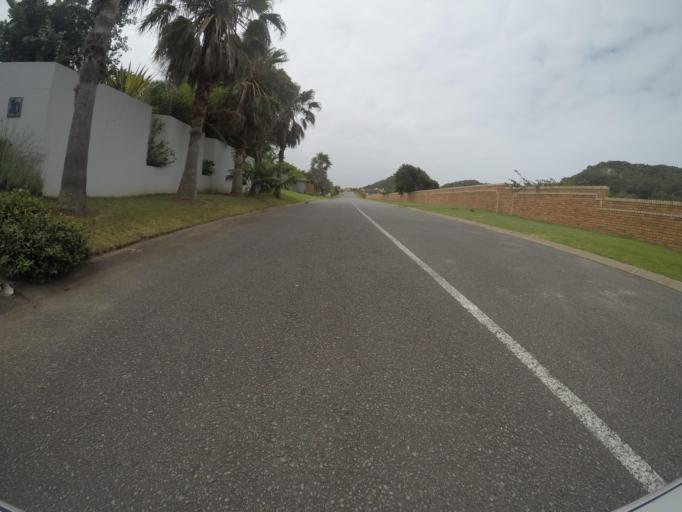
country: ZA
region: Eastern Cape
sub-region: Buffalo City Metropolitan Municipality
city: East London
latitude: -32.9808
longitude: 27.9533
